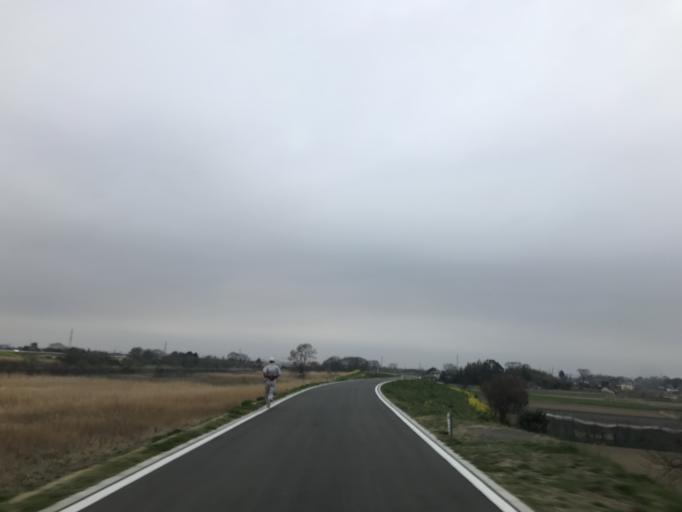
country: JP
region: Ibaraki
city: Mitsukaido
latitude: 36.0262
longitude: 140.0107
